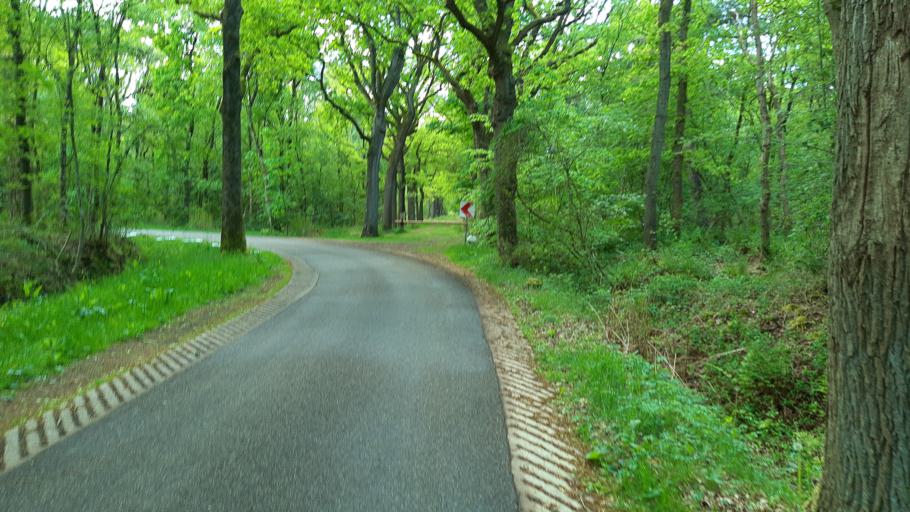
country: NL
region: Friesland
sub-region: Gemeente Gaasterlan-Sleat
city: Balk
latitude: 52.8752
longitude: 5.5605
